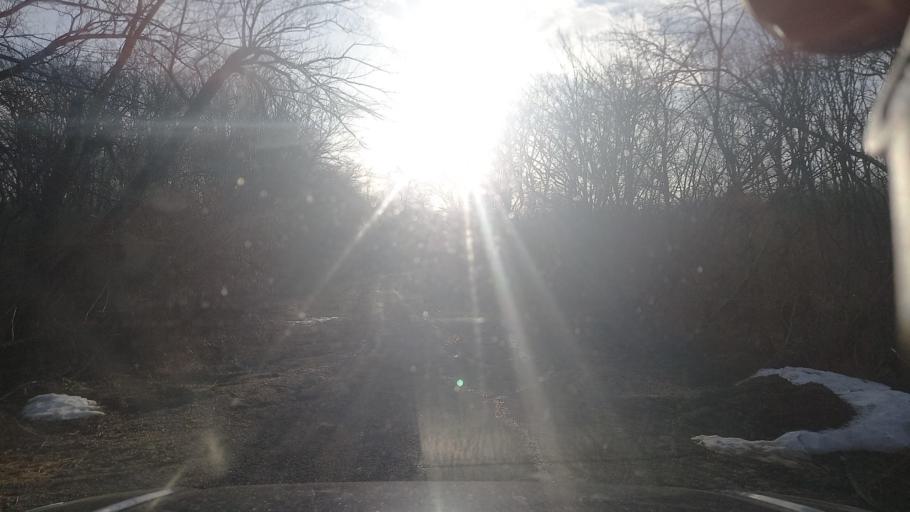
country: RU
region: Krasnodarskiy
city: Novodmitriyevskaya
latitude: 44.6986
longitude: 38.9665
